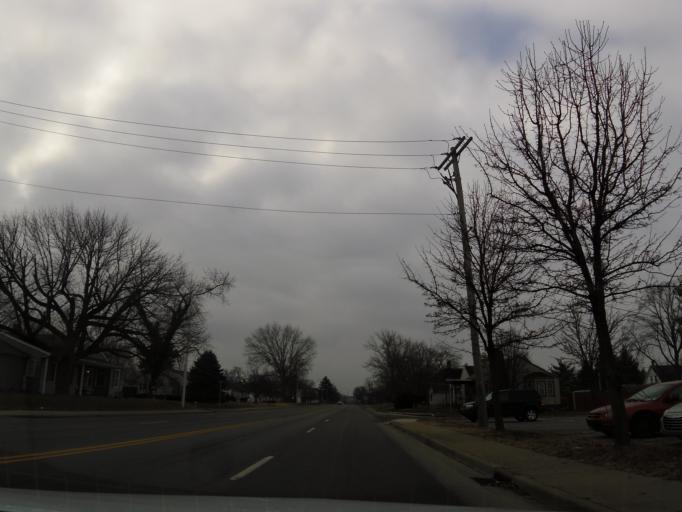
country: US
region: Indiana
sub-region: Bartholomew County
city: Columbus
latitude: 39.2131
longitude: -85.9041
